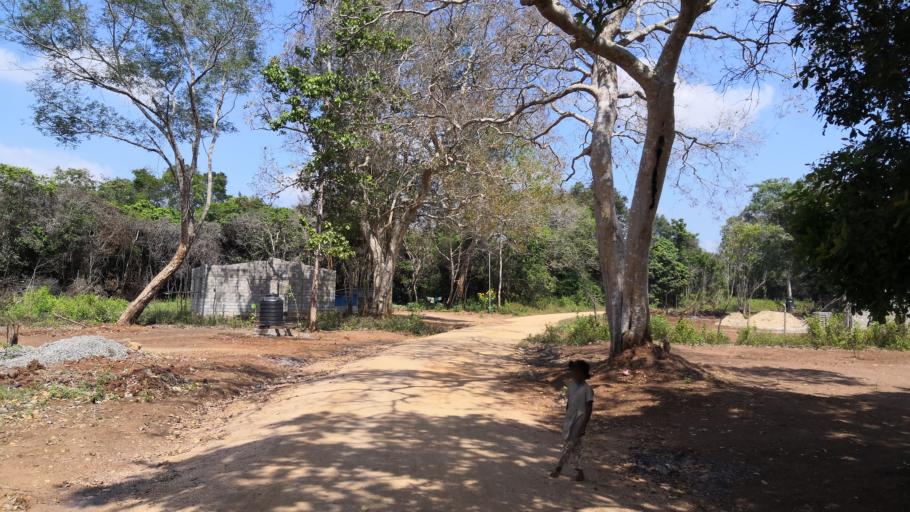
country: LK
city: Padaviya Divisional Secretariat
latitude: 8.9651
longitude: 80.6883
